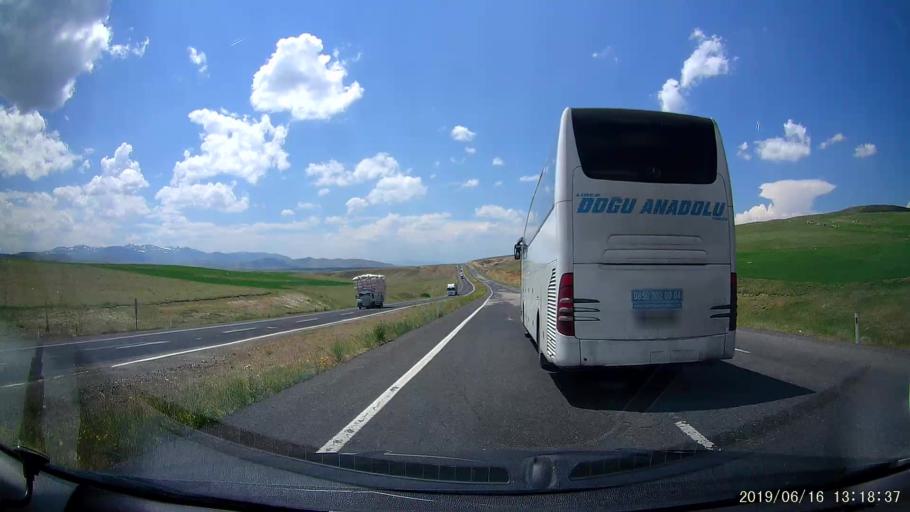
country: TR
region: Agri
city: Taslicay
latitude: 39.6311
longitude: 43.4272
